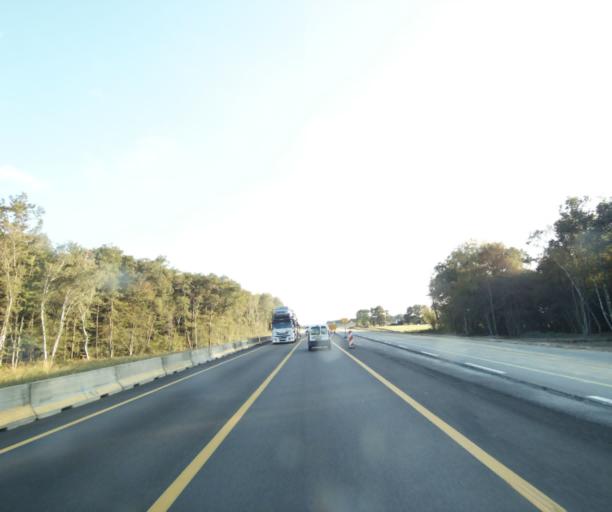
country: FR
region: Bourgogne
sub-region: Departement de Saone-et-Loire
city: Palinges
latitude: 46.5203
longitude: 4.1641
